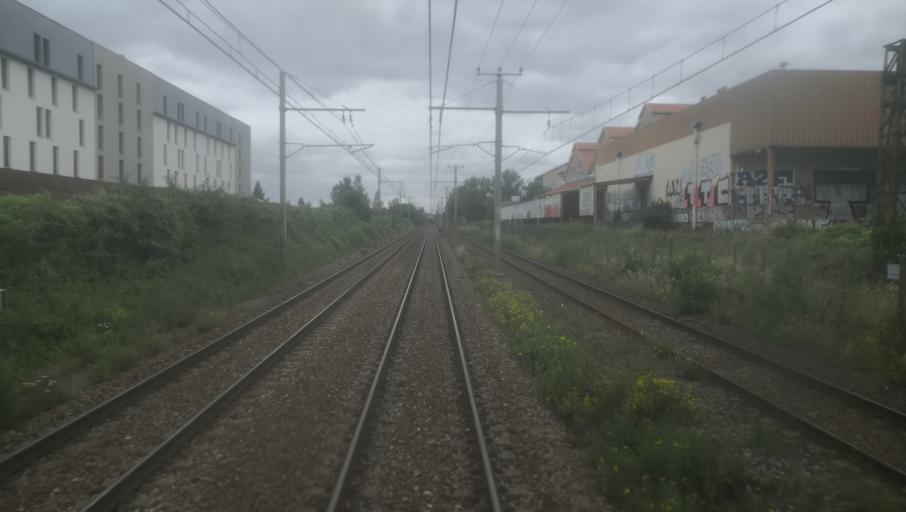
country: FR
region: Midi-Pyrenees
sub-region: Departement de la Haute-Garonne
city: Ramonville-Saint-Agne
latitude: 43.5754
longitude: 1.4773
